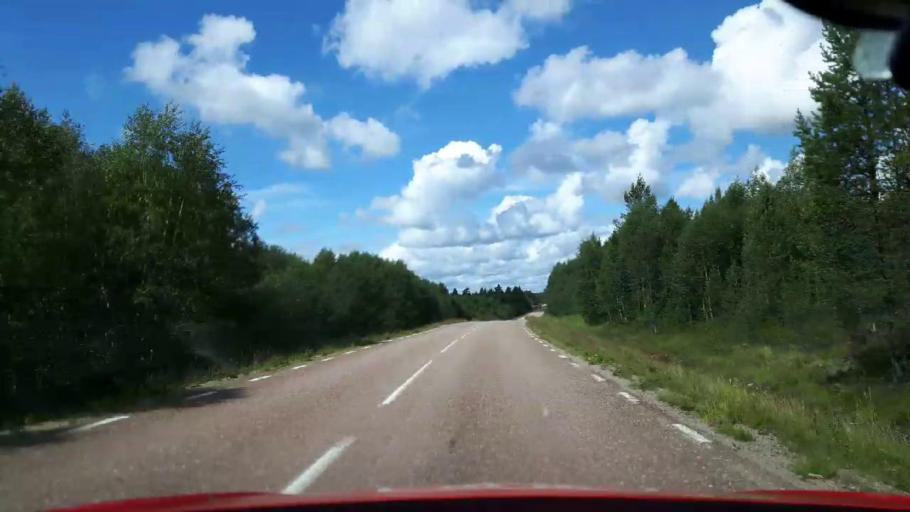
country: SE
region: Dalarna
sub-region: Alvdalens Kommun
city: AElvdalen
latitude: 61.8000
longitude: 13.6697
